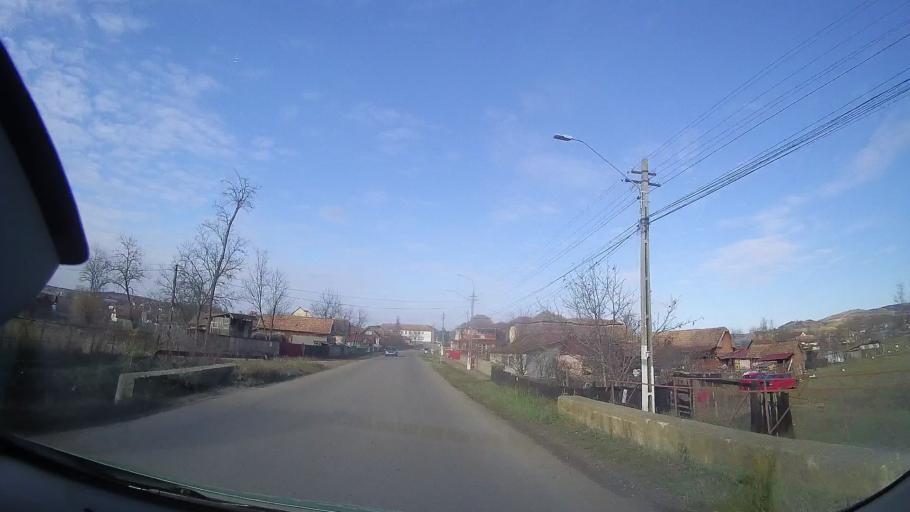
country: RO
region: Mures
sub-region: Comuna Valea Larga
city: Valea Larga
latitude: 46.6192
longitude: 24.0790
